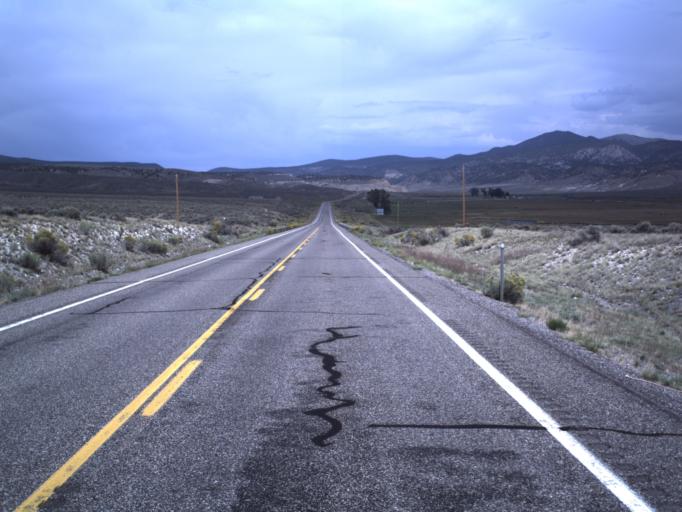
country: US
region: Utah
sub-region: Garfield County
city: Panguitch
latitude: 37.9930
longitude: -112.3909
